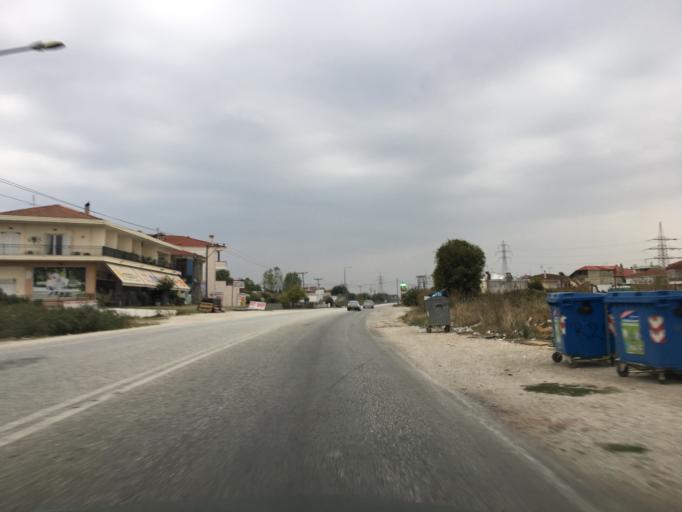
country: GR
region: Thessaly
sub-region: Trikala
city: Trikala
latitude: 39.5643
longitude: 21.7801
